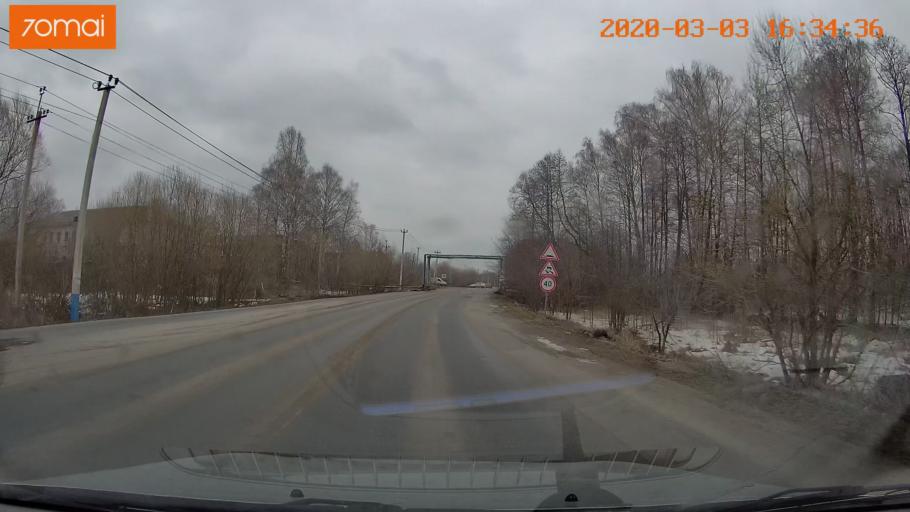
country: RU
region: Moskovskaya
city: Lopatinskiy
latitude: 55.4072
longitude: 38.7593
